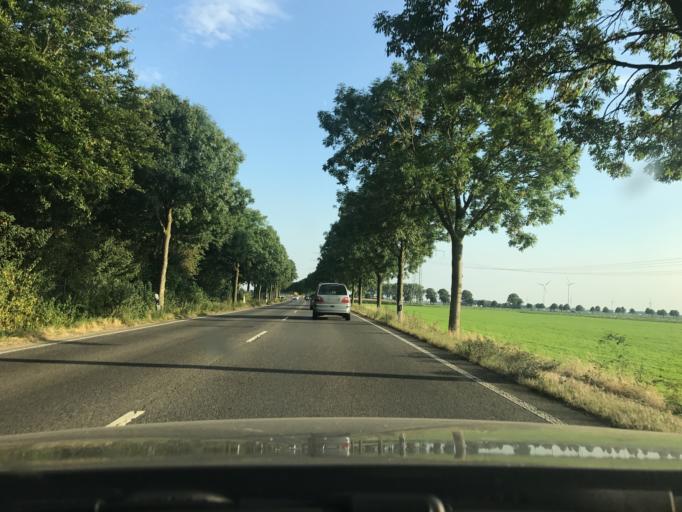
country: DE
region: North Rhine-Westphalia
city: Tonisvorst
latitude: 51.3737
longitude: 6.4910
